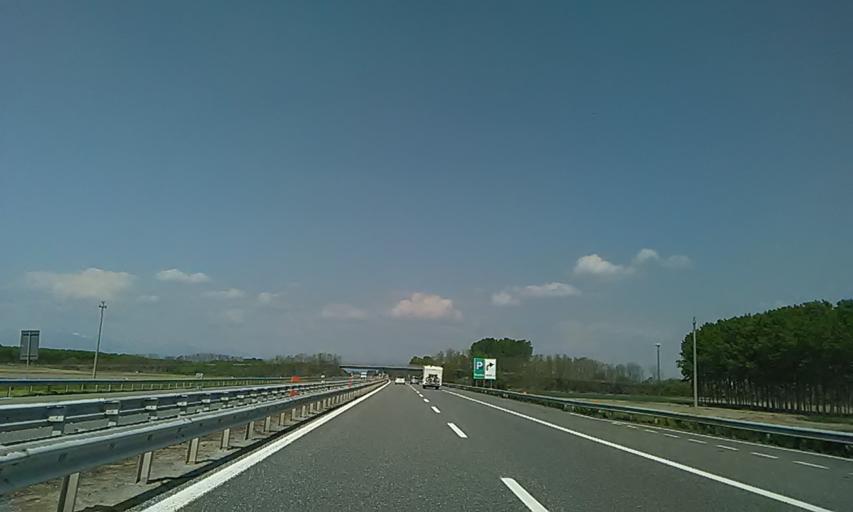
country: IT
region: Piedmont
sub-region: Provincia di Novara
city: Landiona
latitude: 45.4928
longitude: 8.4408
